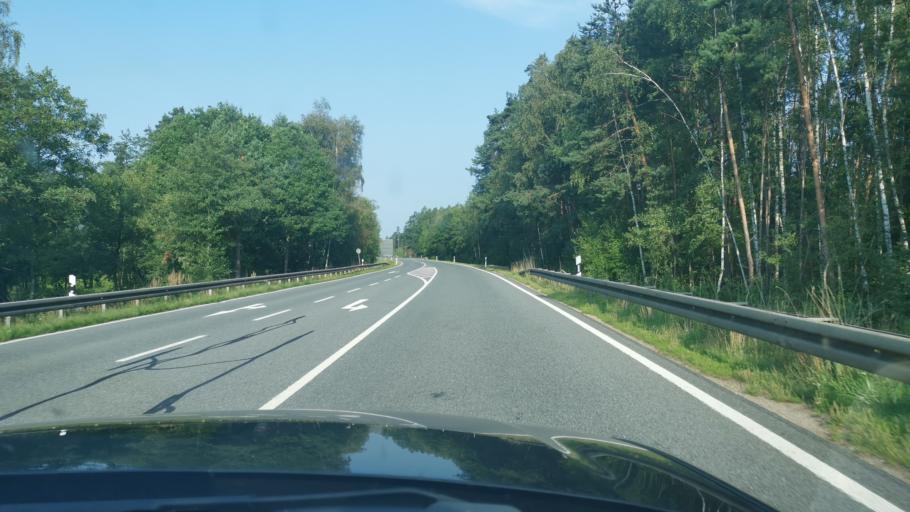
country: DE
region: Bavaria
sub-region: Upper Palatinate
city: Wernberg-Koblitz
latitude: 49.5393
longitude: 12.1171
